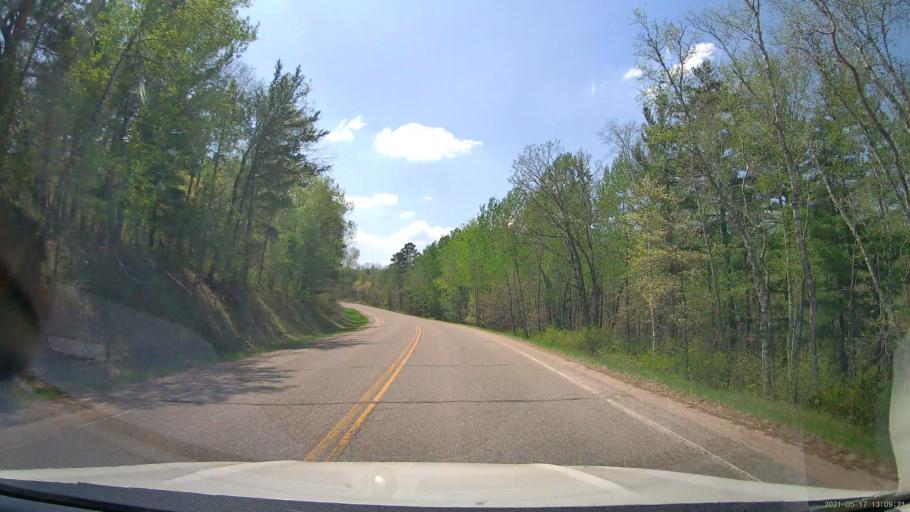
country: US
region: Minnesota
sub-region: Hubbard County
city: Park Rapids
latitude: 47.0279
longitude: -94.9281
